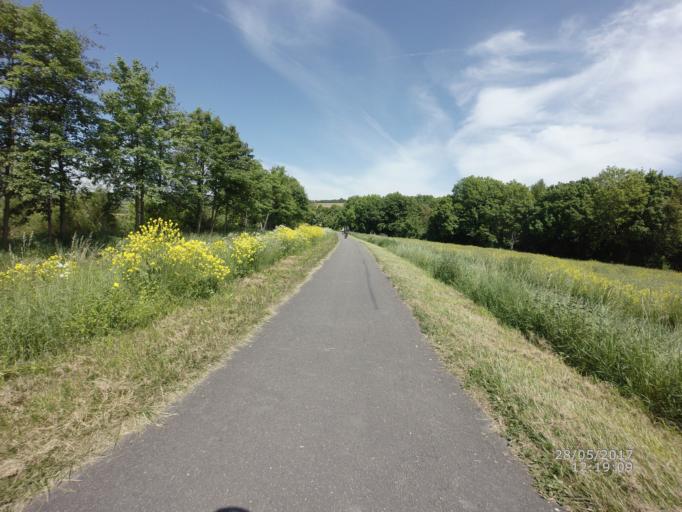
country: DE
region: Thuringia
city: Gorsleben
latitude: 51.2828
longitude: 11.1755
